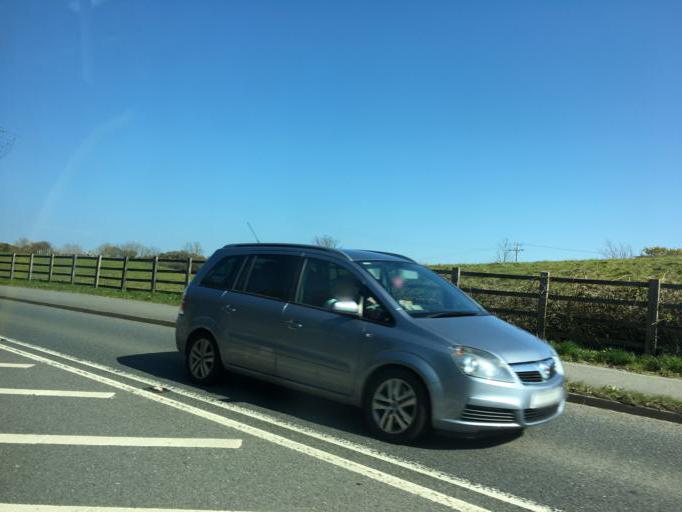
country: GB
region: Wales
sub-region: Gwynedd
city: Y Felinheli
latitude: 53.2010
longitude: -4.1795
